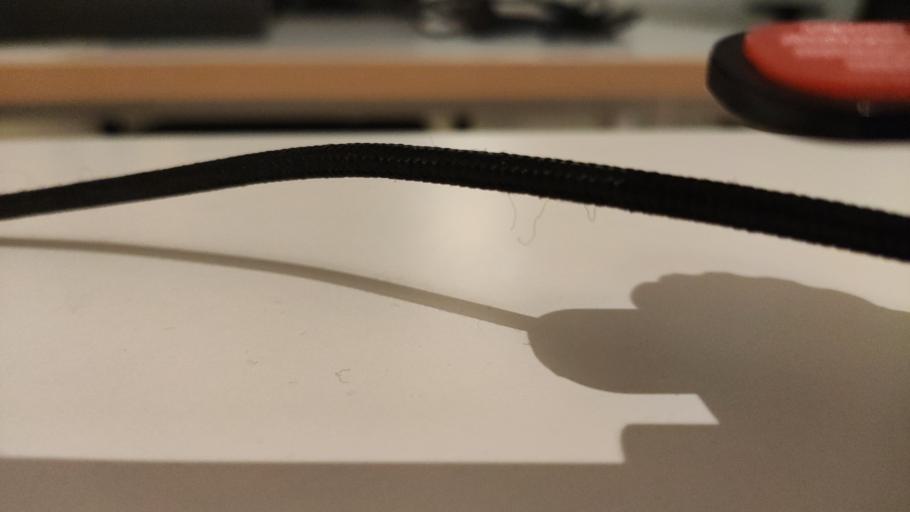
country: RU
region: Moskovskaya
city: Skoropuskovskiy
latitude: 56.3788
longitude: 38.0815
